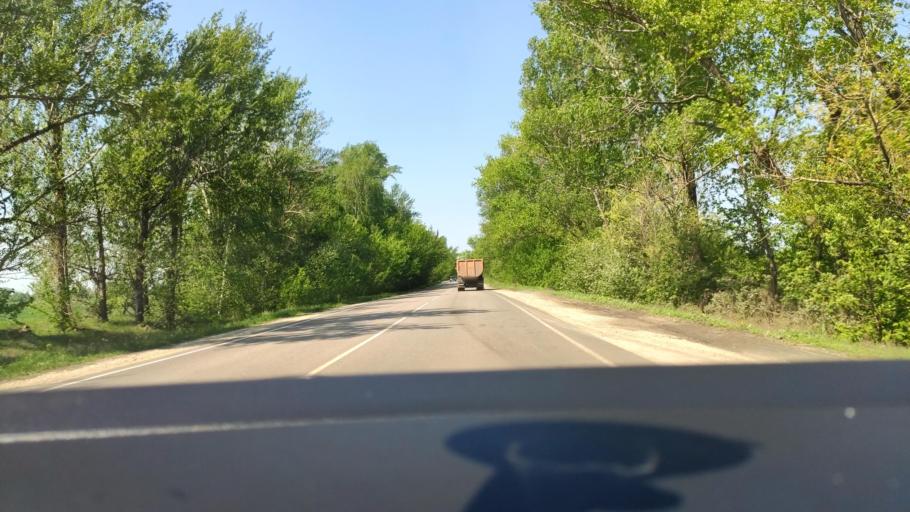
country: RU
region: Voronezj
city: Maslovka
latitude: 51.5304
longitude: 39.3068
